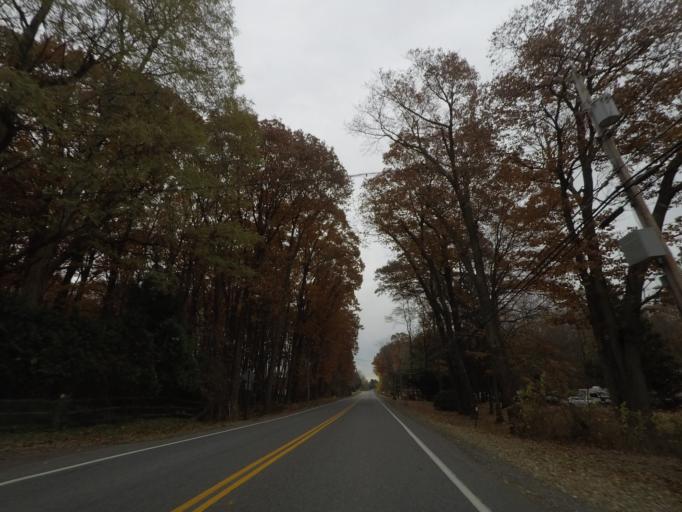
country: US
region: New York
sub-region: Schenectady County
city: Niskayuna
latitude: 42.8047
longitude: -73.8153
